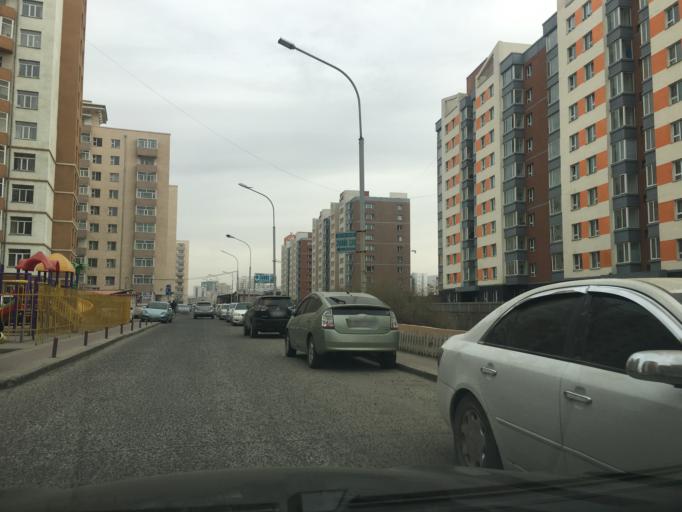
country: MN
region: Ulaanbaatar
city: Ulaanbaatar
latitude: 47.9032
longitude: 106.8861
